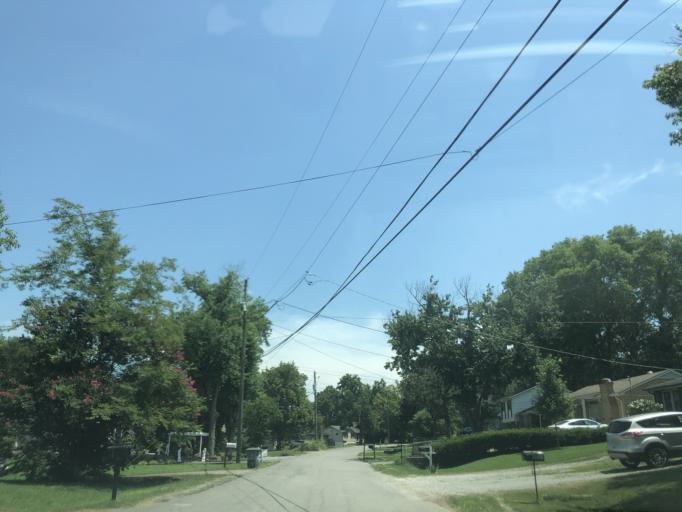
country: US
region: Tennessee
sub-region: Davidson County
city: Lakewood
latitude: 36.1914
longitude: -86.6196
